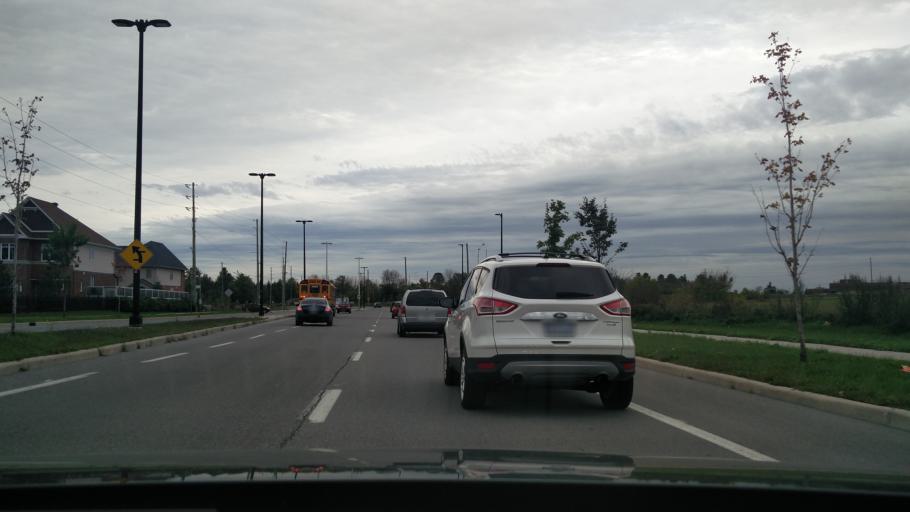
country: CA
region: Ontario
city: Bells Corners
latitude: 45.2665
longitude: -75.7345
